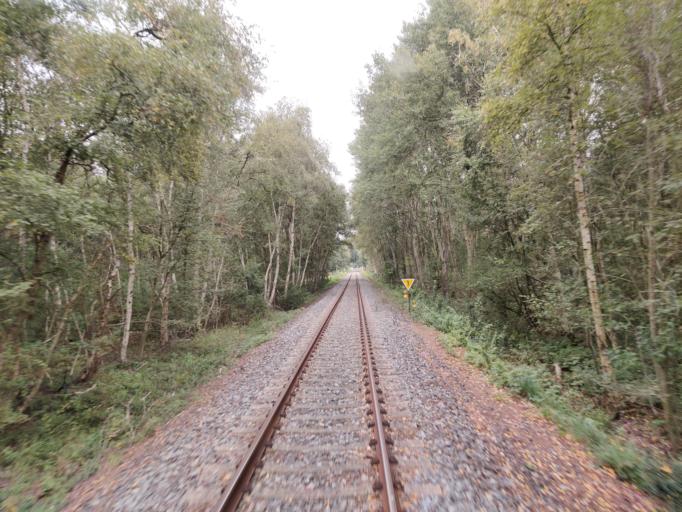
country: DE
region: Lower Saxony
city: Worpswede
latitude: 53.2327
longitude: 8.9392
